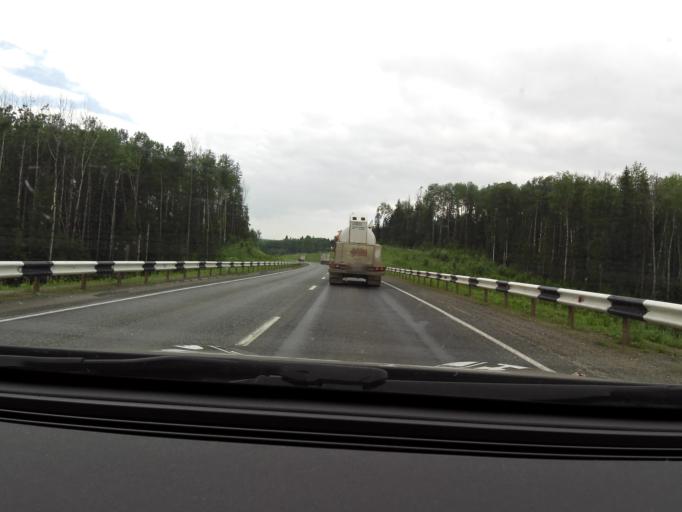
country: RU
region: Perm
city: Suksun
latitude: 57.1067
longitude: 57.3075
